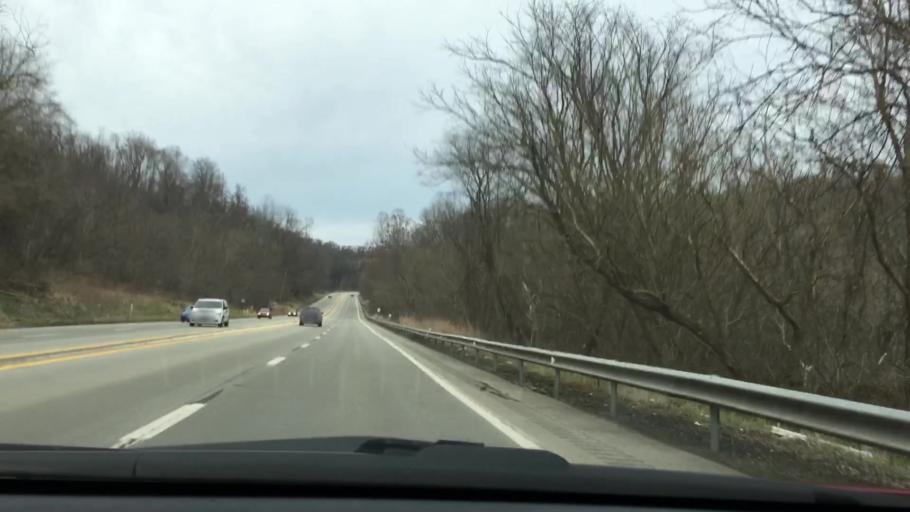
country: US
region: Pennsylvania
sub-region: Fayette County
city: Perryopolis
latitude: 40.0069
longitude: -79.7624
